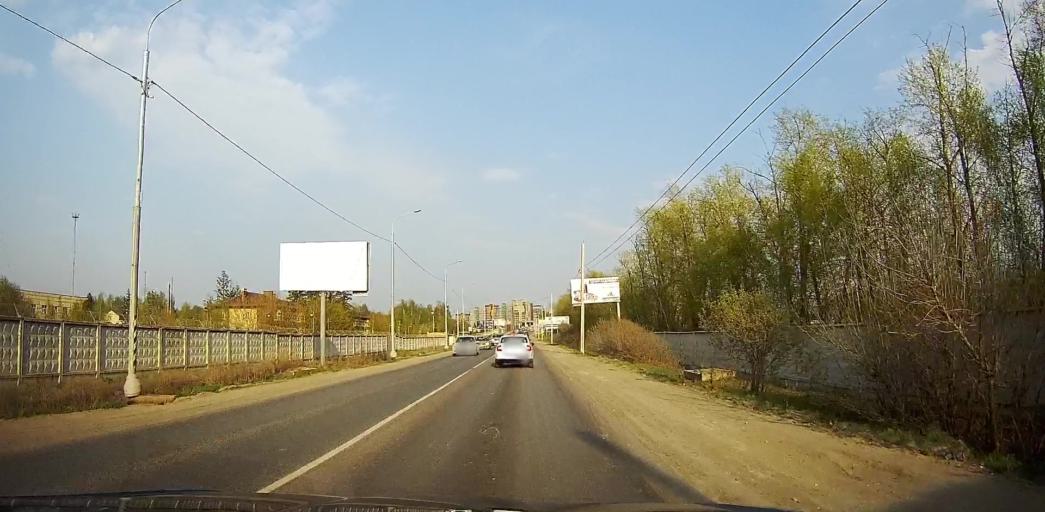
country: RU
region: Moskovskaya
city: Petrovskaya
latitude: 55.5606
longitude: 37.7957
